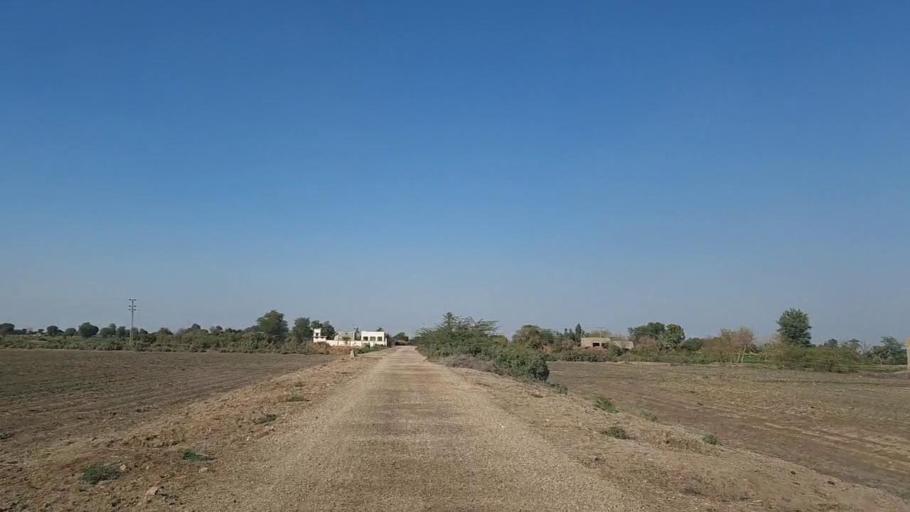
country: PK
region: Sindh
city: Shahpur Chakar
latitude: 26.2206
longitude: 68.6348
